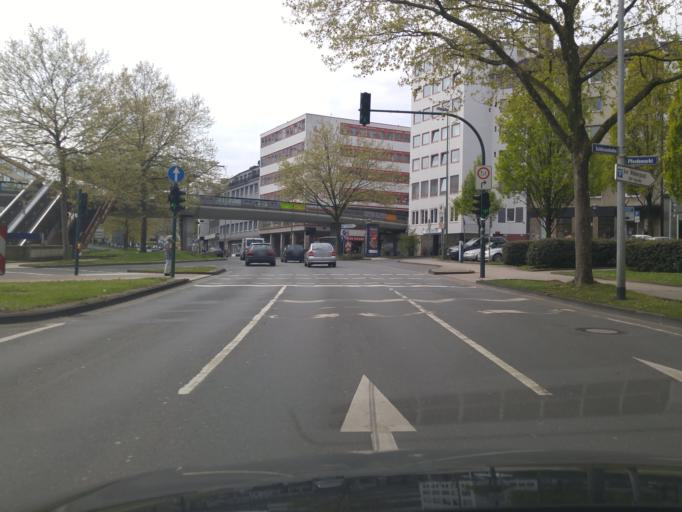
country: DE
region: North Rhine-Westphalia
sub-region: Regierungsbezirk Dusseldorf
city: Essen
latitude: 51.4614
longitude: 7.0150
